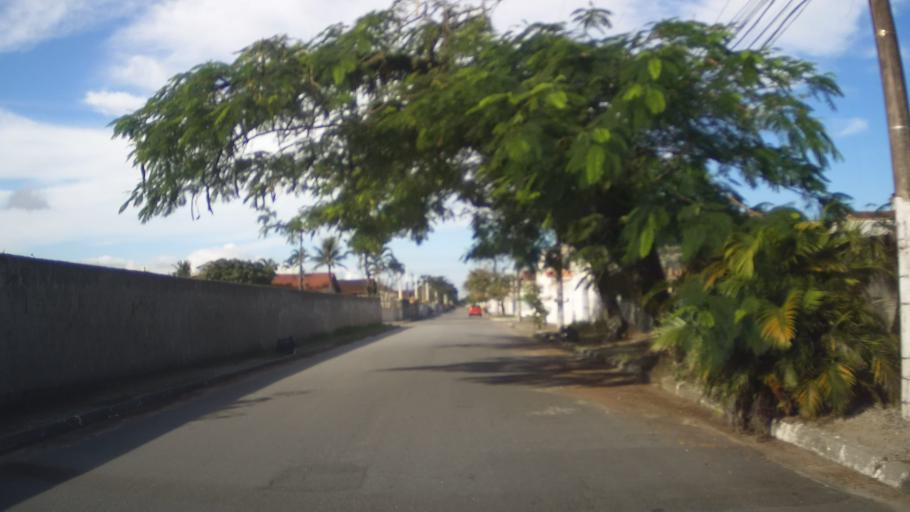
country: BR
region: Sao Paulo
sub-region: Itanhaem
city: Itanhaem
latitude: -24.1644
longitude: -46.7517
